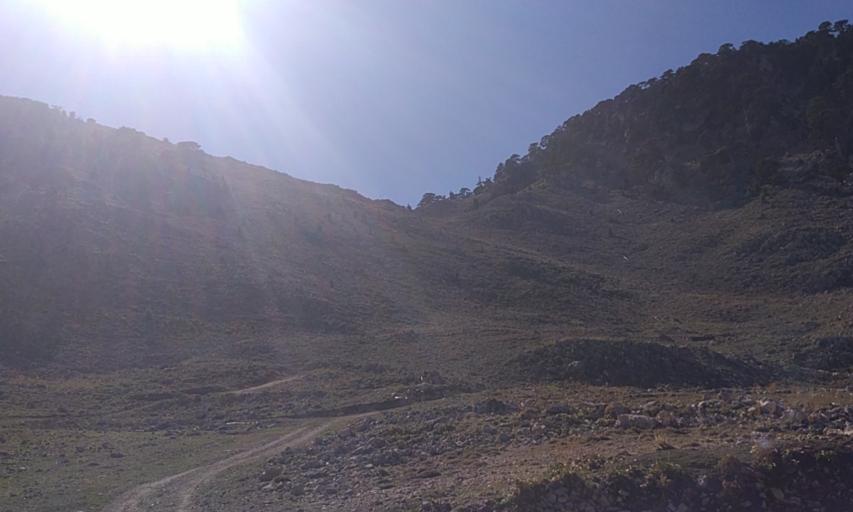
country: TR
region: Antalya
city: Altinyaka
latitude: 36.5481
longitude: 30.4113
